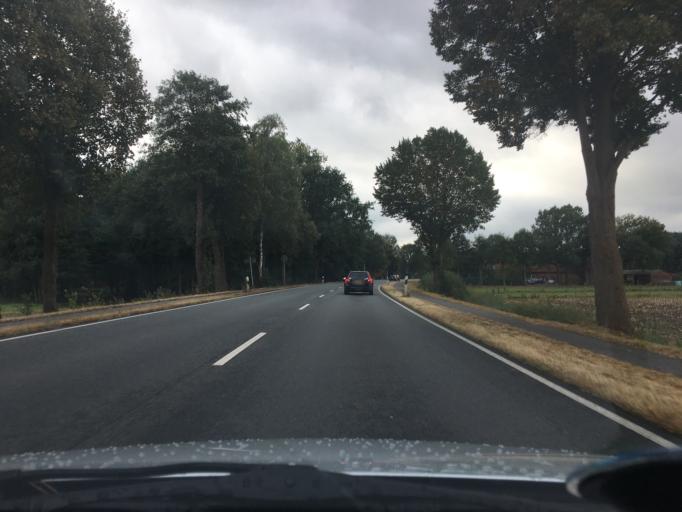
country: DE
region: Lower Saxony
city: Alfhausen
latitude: 52.4955
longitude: 7.9588
